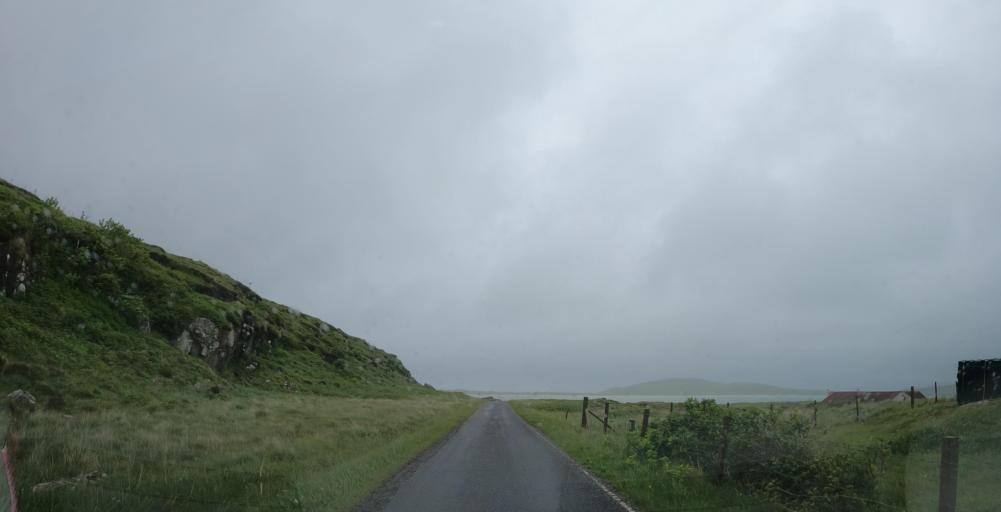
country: GB
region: Scotland
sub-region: Eilean Siar
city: Barra
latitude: 57.0143
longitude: -7.4314
